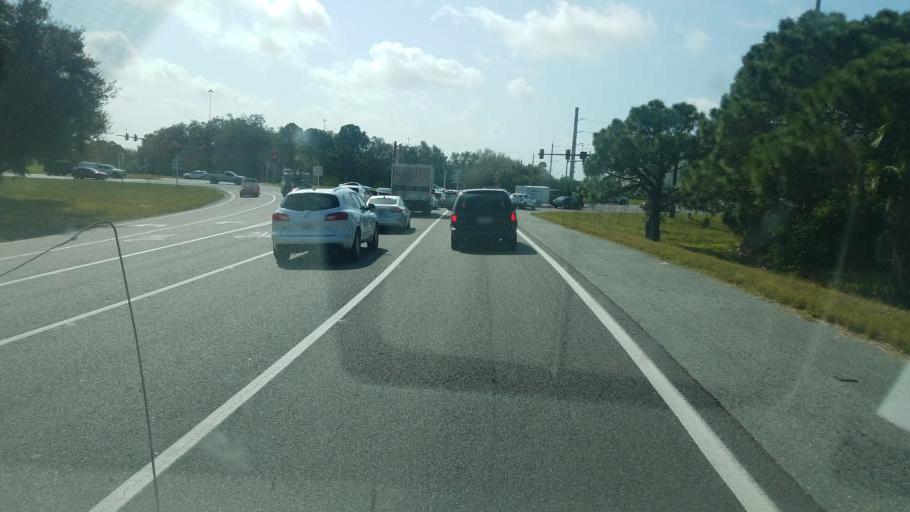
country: US
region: Florida
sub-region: Sarasota County
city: Fruitville
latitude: 27.3392
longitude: -82.4489
